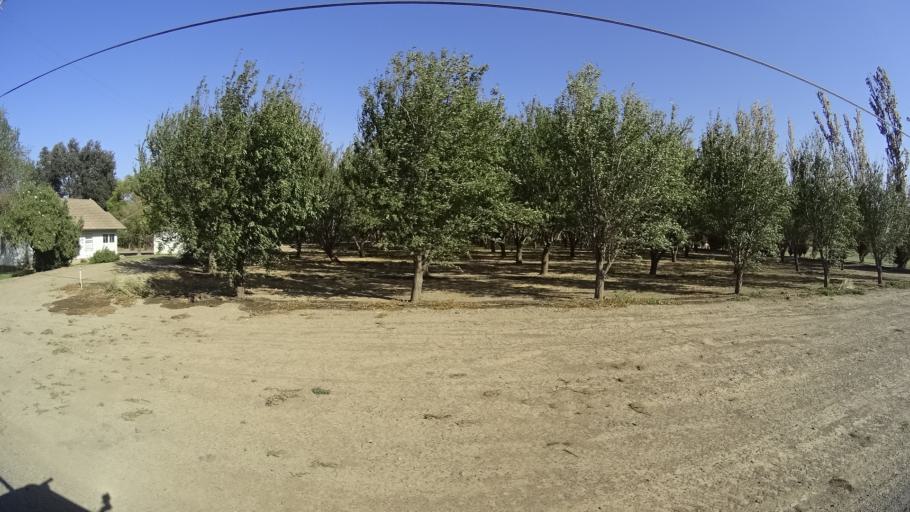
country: US
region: California
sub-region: Yolo County
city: Woodland
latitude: 38.7457
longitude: -121.8027
